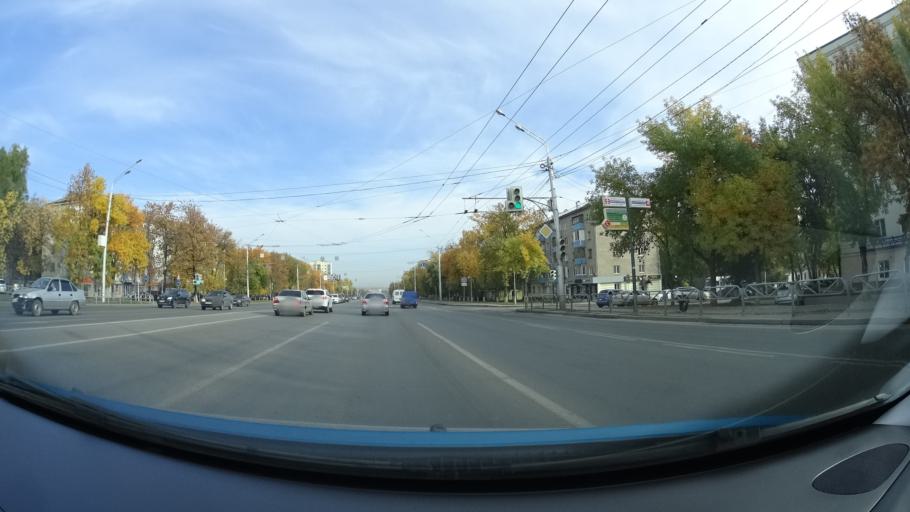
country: RU
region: Bashkortostan
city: Ufa
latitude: 54.7902
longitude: 56.0363
